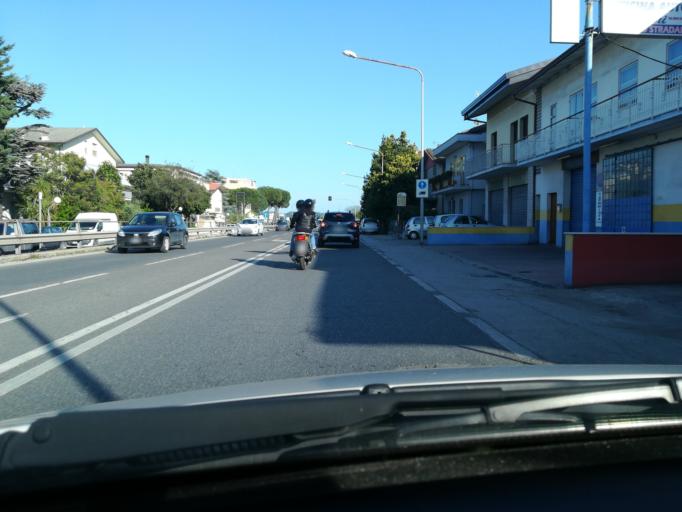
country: IT
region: Emilia-Romagna
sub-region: Provincia di Rimini
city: Misano Adriatico
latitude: 43.9745
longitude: 12.6950
